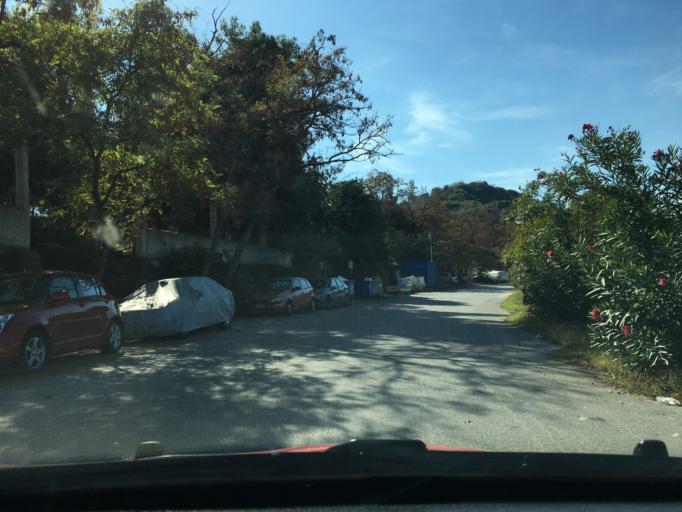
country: GR
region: Central Macedonia
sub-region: Nomos Chalkidikis
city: Ierissos
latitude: 40.3936
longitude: 23.8939
